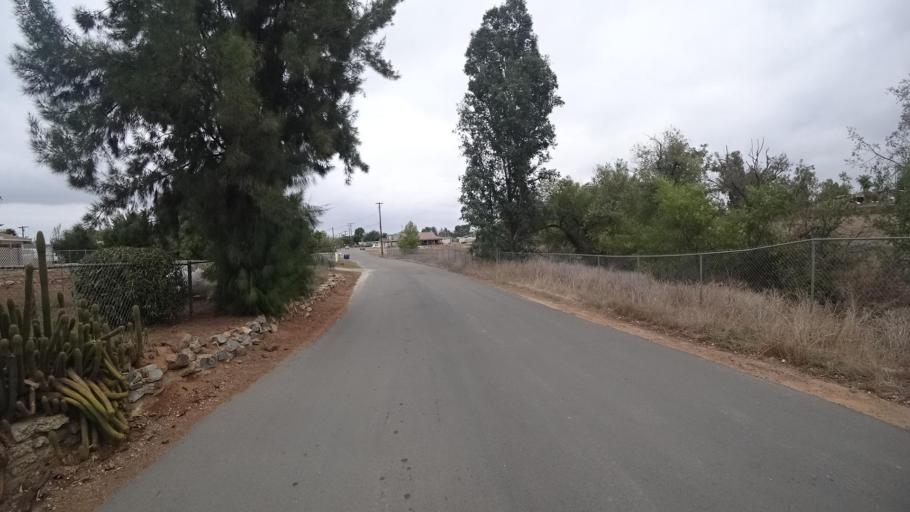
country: US
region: California
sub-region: San Diego County
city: Ramona
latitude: 33.0237
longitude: -116.8921
